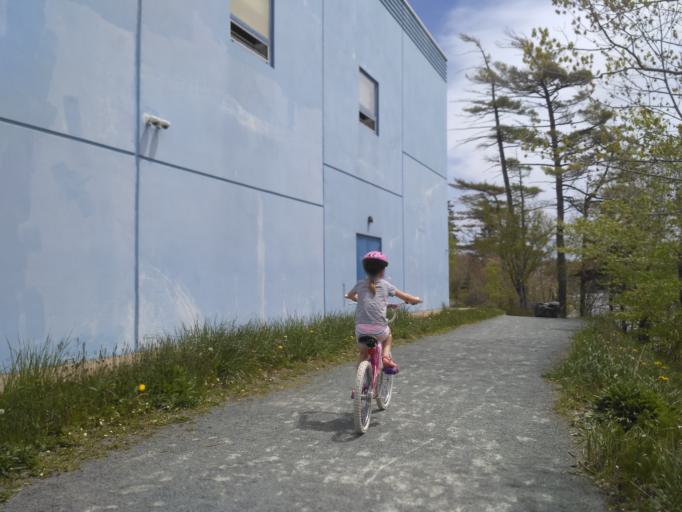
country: CA
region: Nova Scotia
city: Dartmouth
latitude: 44.7769
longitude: -63.6679
